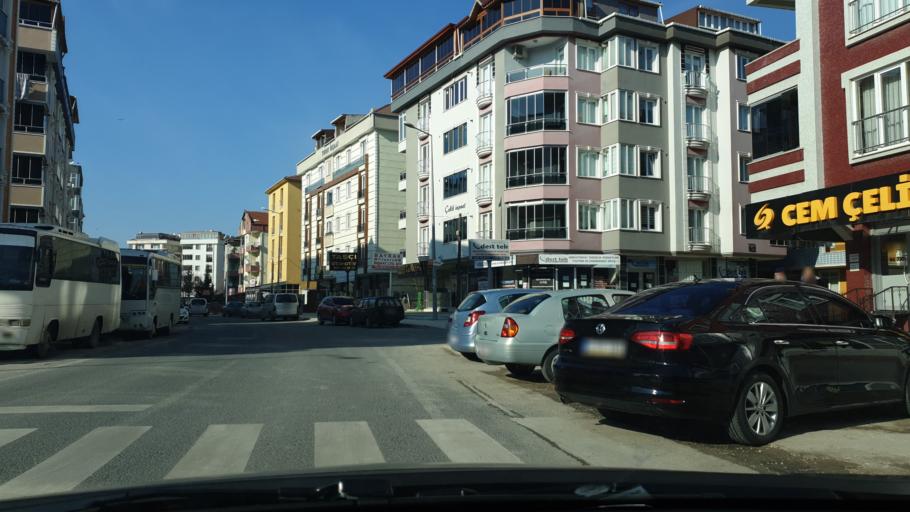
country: TR
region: Tekirdag
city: Cerkezkoey
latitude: 41.2862
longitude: 27.9932
